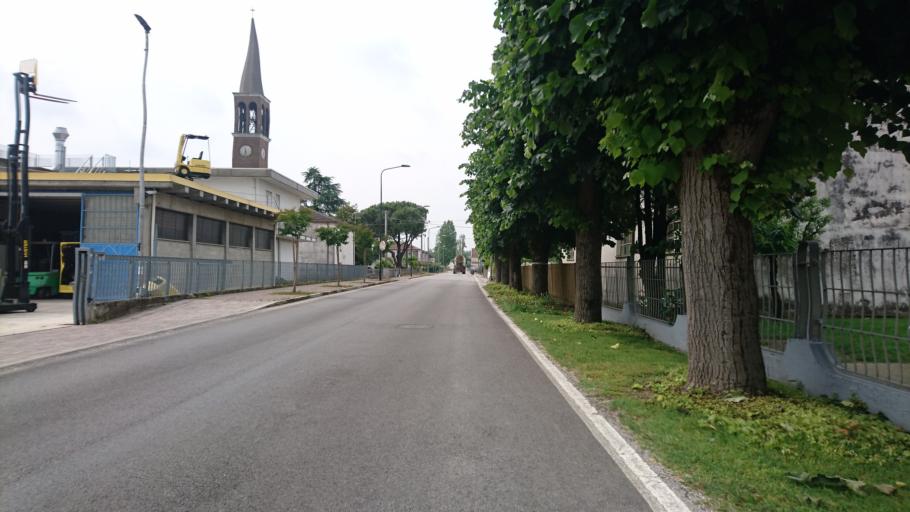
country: IT
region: Veneto
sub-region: Provincia di Rovigo
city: Lendinara
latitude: 45.1129
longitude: 11.6192
